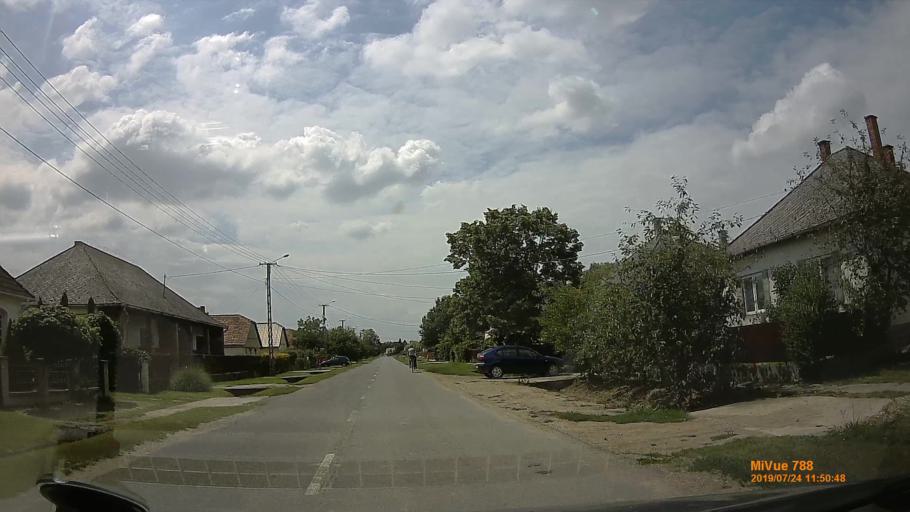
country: UA
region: Zakarpattia
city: Batiovo
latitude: 48.2384
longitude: 22.4355
